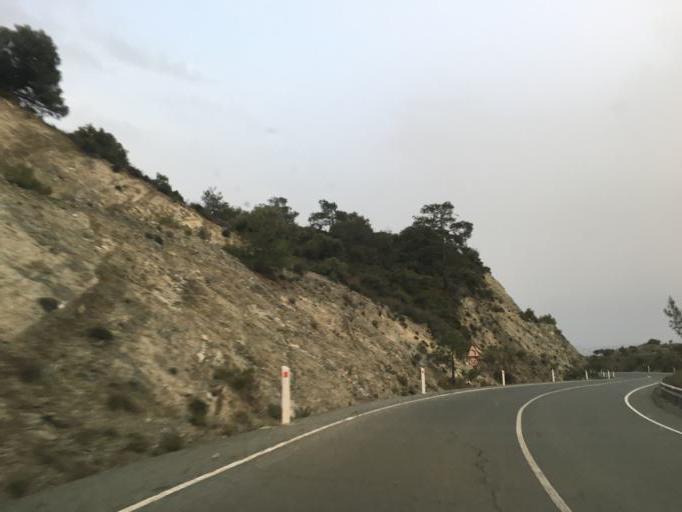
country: CY
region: Limassol
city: Parekklisha
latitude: 34.8026
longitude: 33.1486
